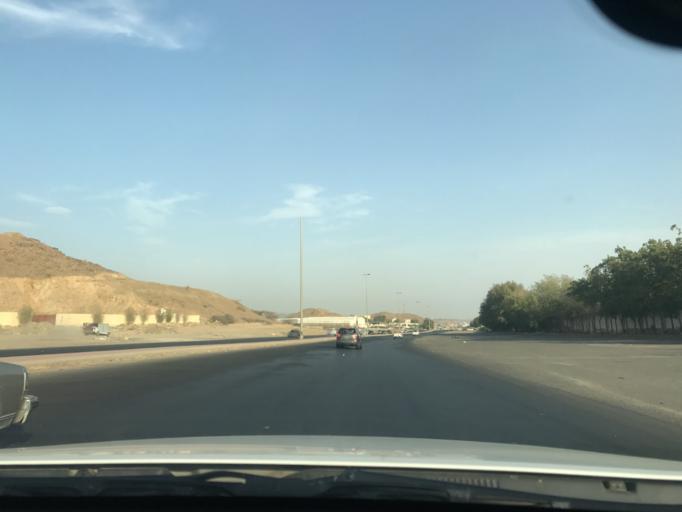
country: SA
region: Makkah
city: Jeddah
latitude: 21.4095
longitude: 39.4247
